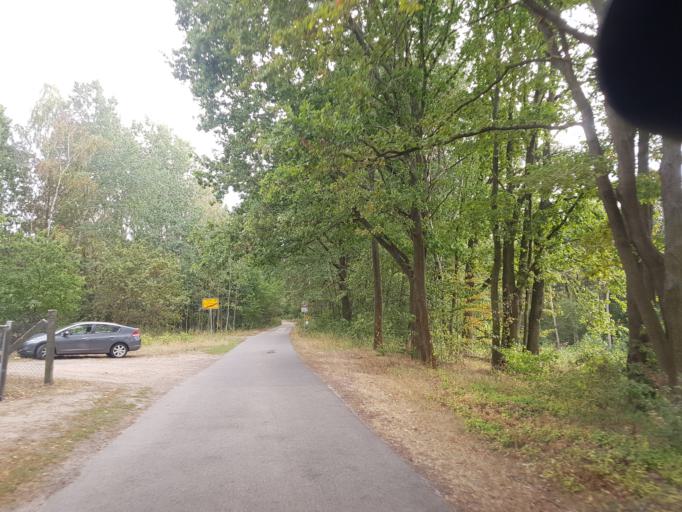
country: DE
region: Brandenburg
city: Calau
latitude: 51.7155
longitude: 13.9480
